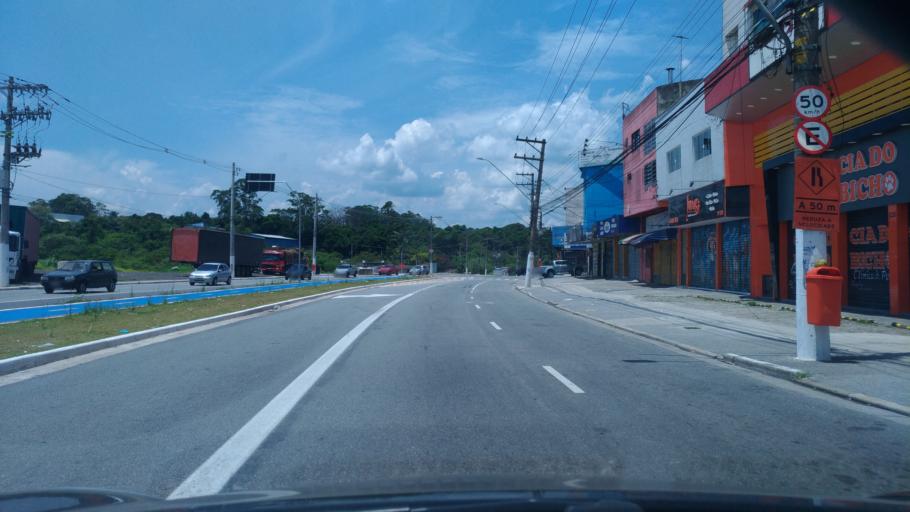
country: BR
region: Sao Paulo
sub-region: Sao Bernardo Do Campo
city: Sao Bernardo do Campo
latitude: -23.7375
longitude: -46.5913
